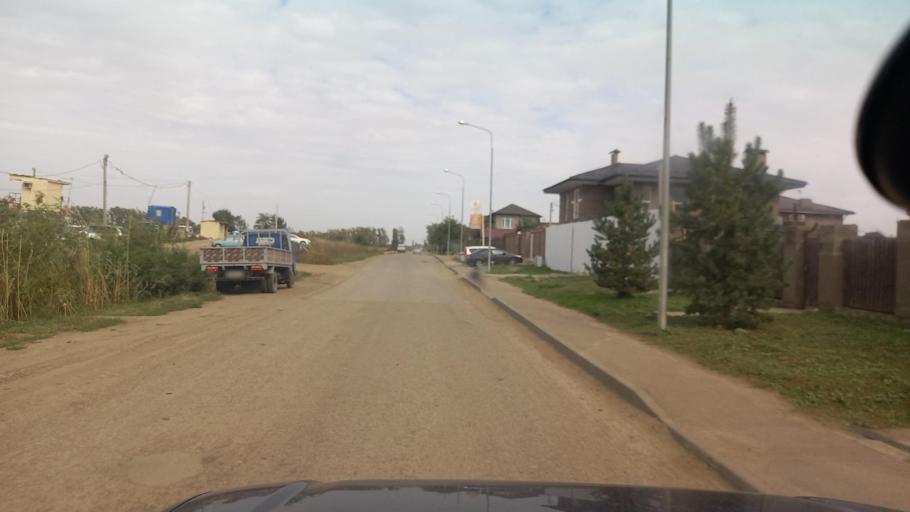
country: RU
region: Krasnodarskiy
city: Krasnodar
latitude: 45.1238
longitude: 38.9212
